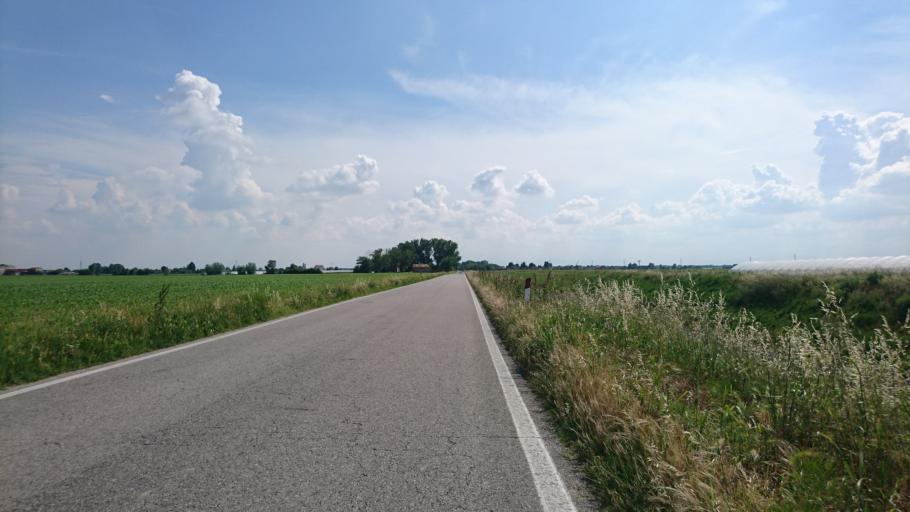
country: IT
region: Veneto
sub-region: Provincia di Rovigo
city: Castelmassa
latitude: 45.0486
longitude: 11.3238
